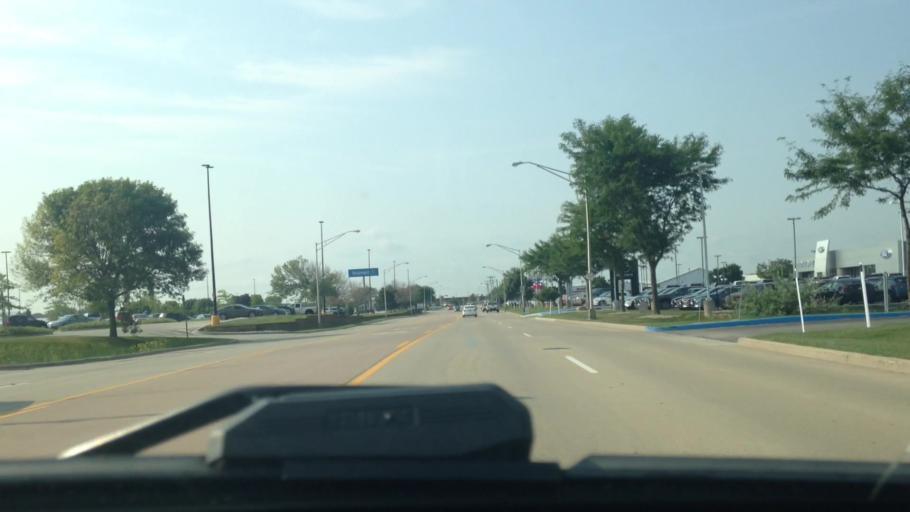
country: US
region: Wisconsin
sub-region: Fond du Lac County
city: North Fond du Lac
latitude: 43.7894
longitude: -88.4865
